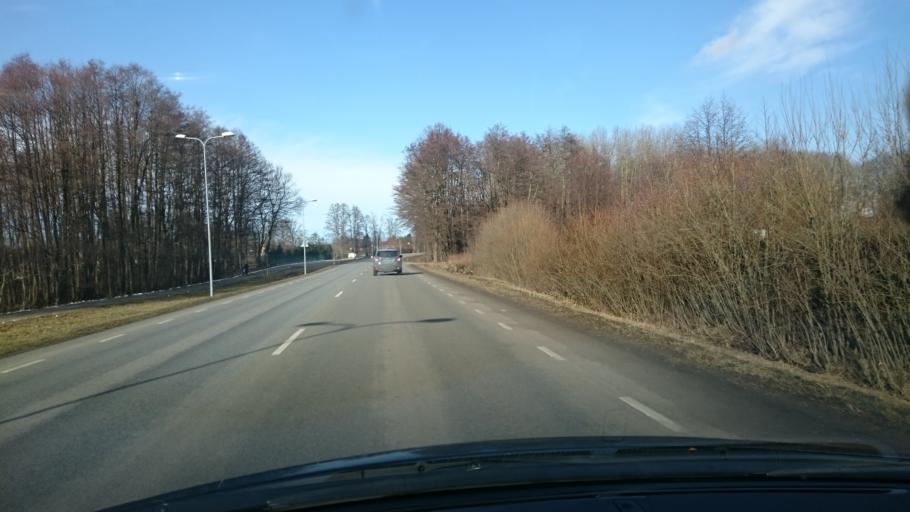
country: EE
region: Harju
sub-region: Keila linn
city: Keila
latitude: 59.4399
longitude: 24.3716
